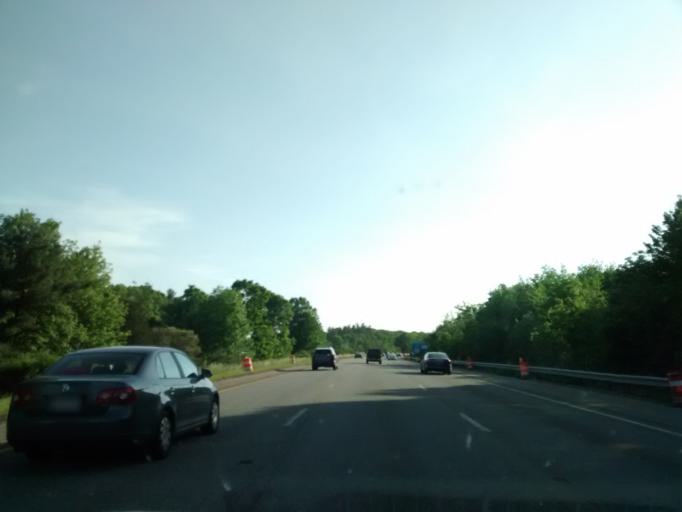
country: US
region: Massachusetts
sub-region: Worcester County
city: Northborough
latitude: 42.3354
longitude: -71.6627
